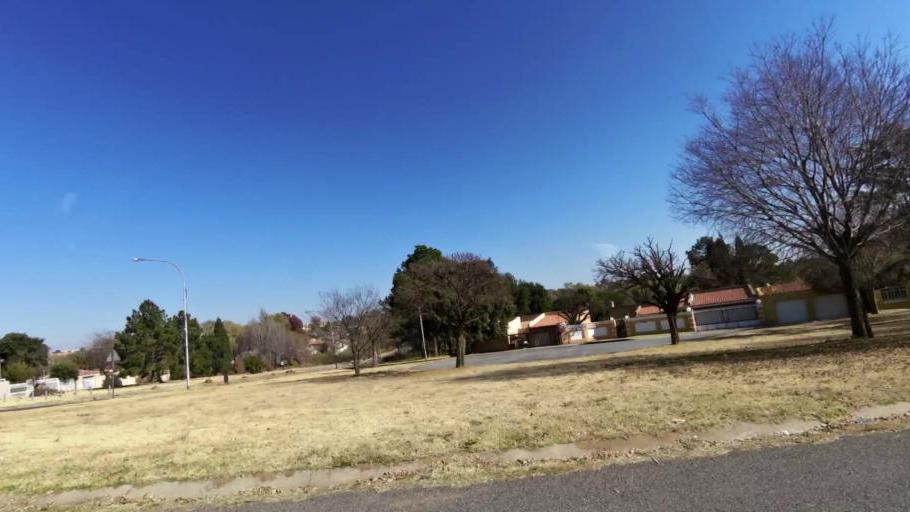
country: ZA
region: Gauteng
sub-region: City of Johannesburg Metropolitan Municipality
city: Johannesburg
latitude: -26.2466
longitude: 27.9924
